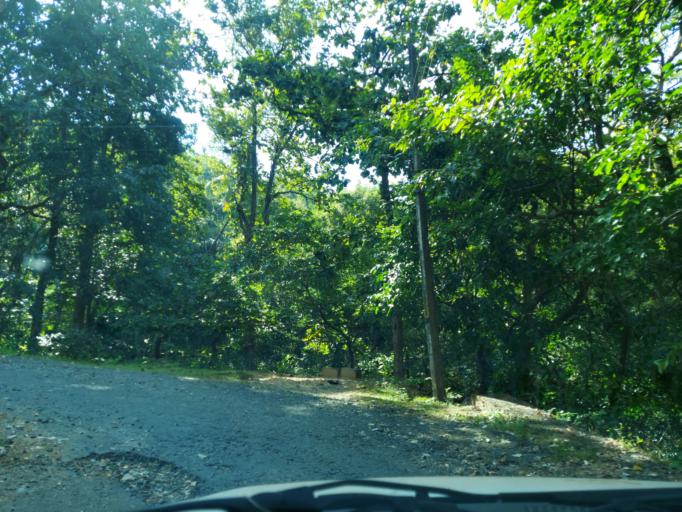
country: IN
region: Maharashtra
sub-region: Sindhudurg
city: Savantvadi
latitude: 15.9049
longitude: 73.8132
